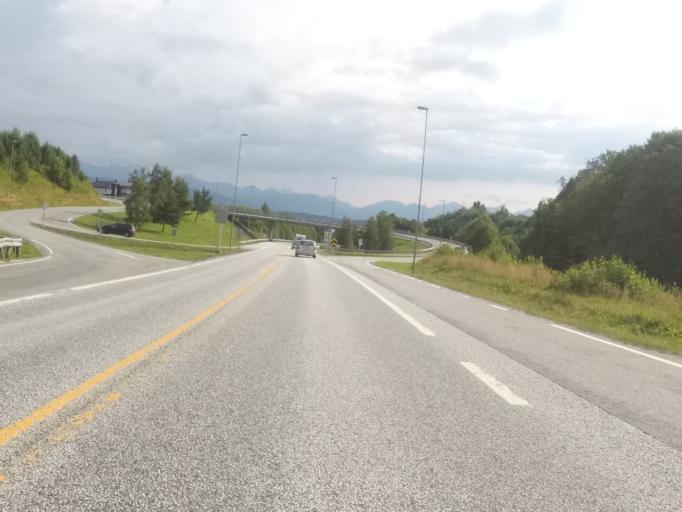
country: NO
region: More og Romsdal
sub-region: Molde
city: Molde
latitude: 62.7533
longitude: 7.2635
